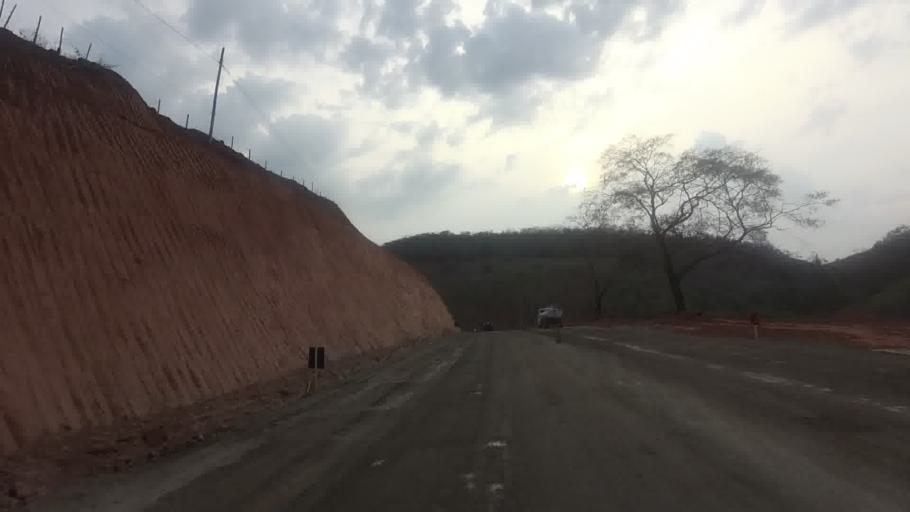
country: BR
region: Rio de Janeiro
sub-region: Santo Antonio De Padua
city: Santo Antonio de Padua
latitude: -21.5104
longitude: -42.0895
